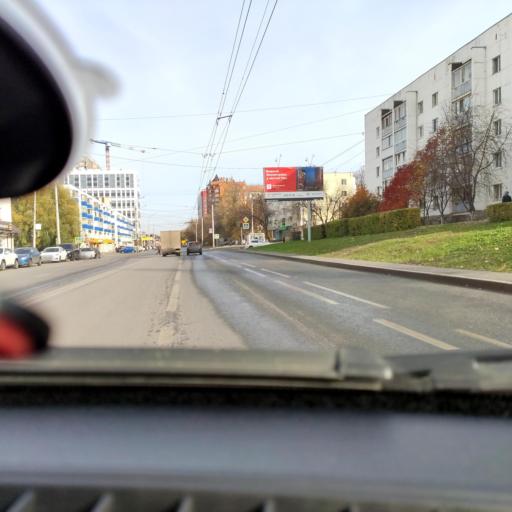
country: RU
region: Bashkortostan
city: Ufa
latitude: 54.7264
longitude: 55.9284
